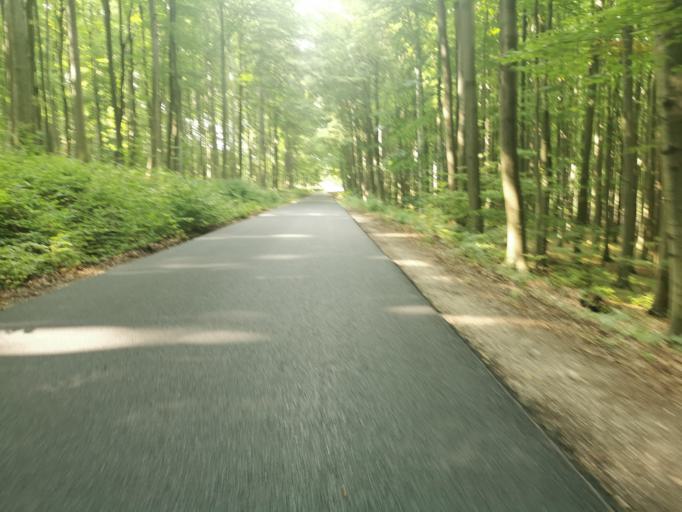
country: SK
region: Trenciansky
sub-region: Okres Myjava
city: Myjava
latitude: 48.8039
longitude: 17.6034
